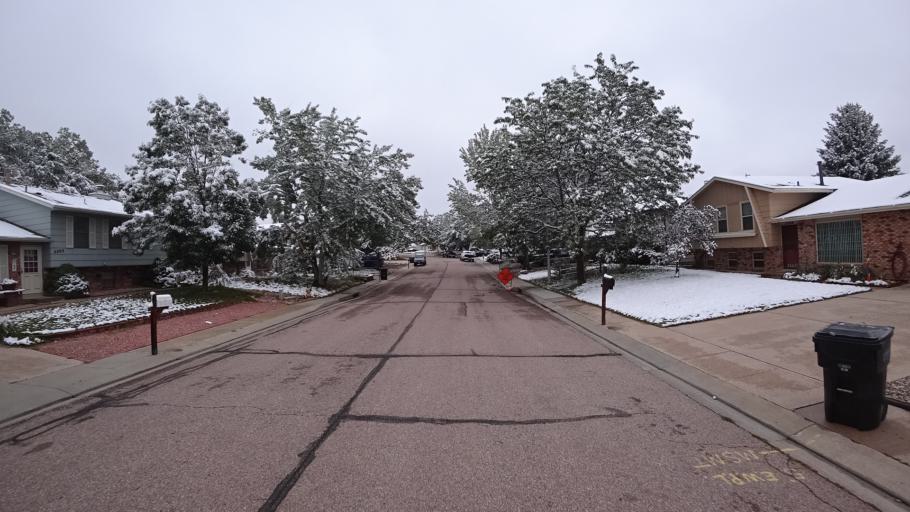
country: US
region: Colorado
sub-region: El Paso County
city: Colorado Springs
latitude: 38.9236
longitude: -104.7896
